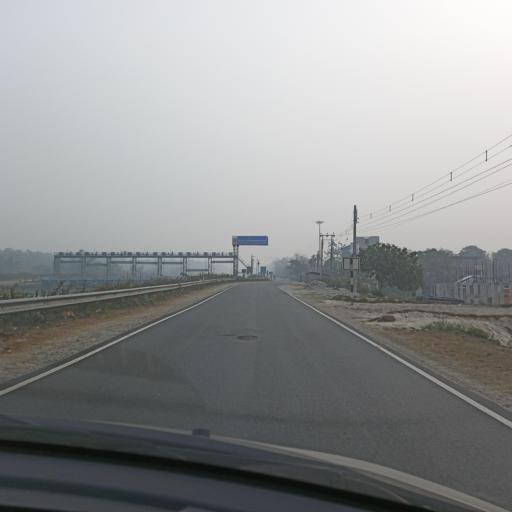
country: IN
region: West Bengal
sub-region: Darjiling
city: Shiliguri
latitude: 26.6816
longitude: 88.5608
